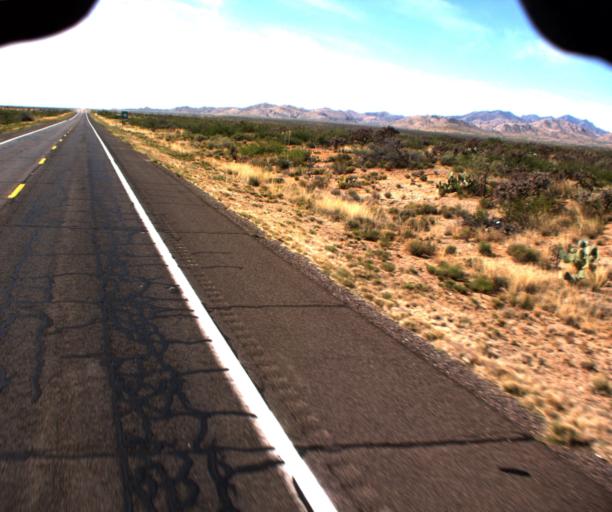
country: US
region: Arizona
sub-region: Graham County
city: Swift Trail Junction
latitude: 32.6060
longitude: -109.6867
